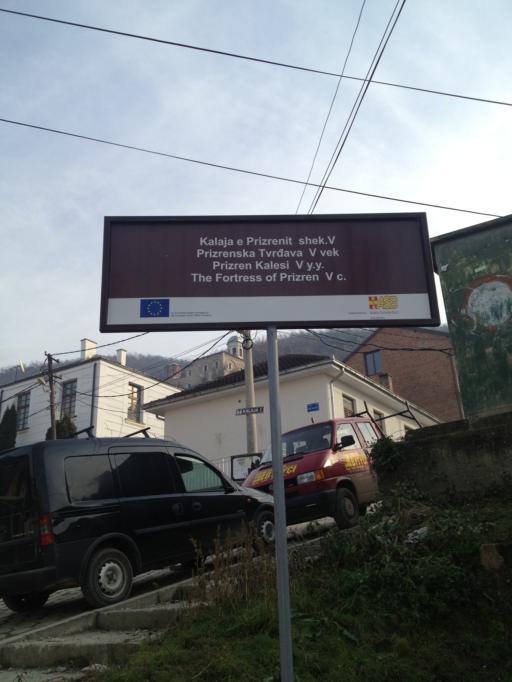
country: XK
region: Prizren
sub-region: Prizren
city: Prizren
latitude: 42.2087
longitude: 20.7418
